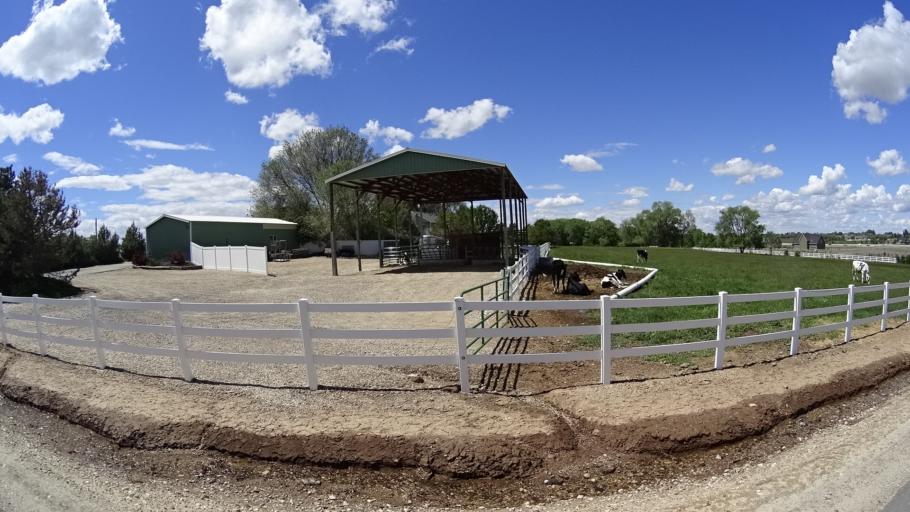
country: US
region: Idaho
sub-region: Ada County
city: Meridian
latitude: 43.5721
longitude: -116.4535
